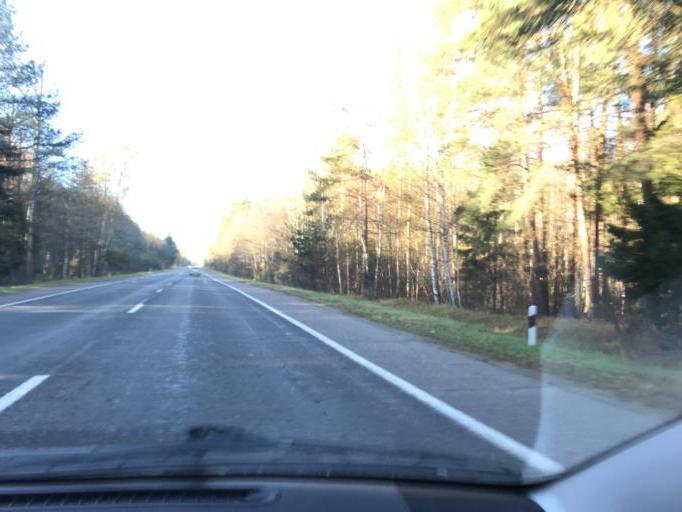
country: BY
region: Vitebsk
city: Syanno
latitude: 55.0729
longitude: 29.5543
